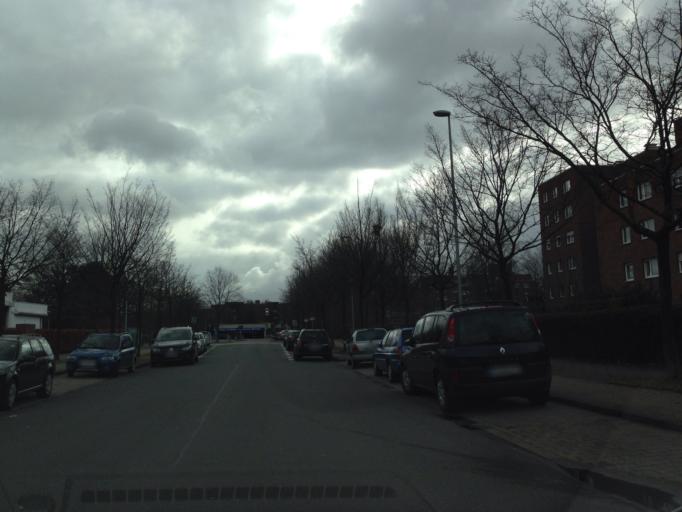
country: DE
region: North Rhine-Westphalia
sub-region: Regierungsbezirk Munster
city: Muenster
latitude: 51.9984
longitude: 7.6033
